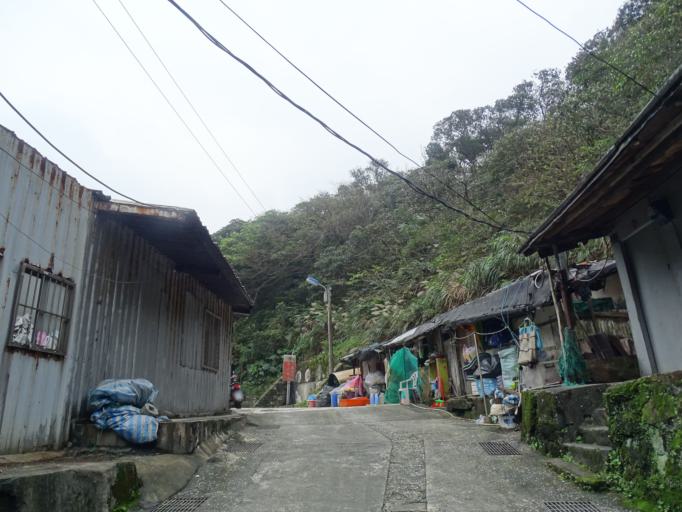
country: TW
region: Taiwan
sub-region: Keelung
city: Keelung
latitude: 25.1582
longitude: 121.7711
